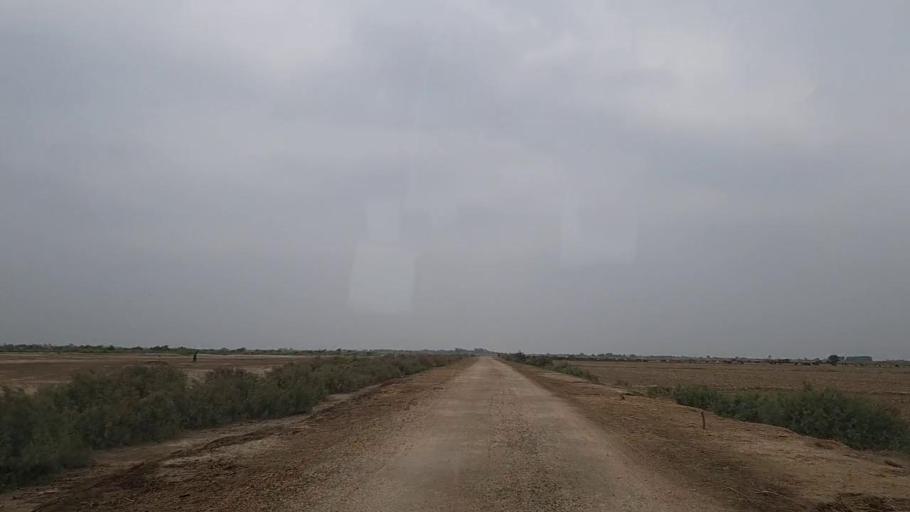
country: PK
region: Sindh
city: Mirpur Sakro
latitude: 24.6265
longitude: 67.7189
